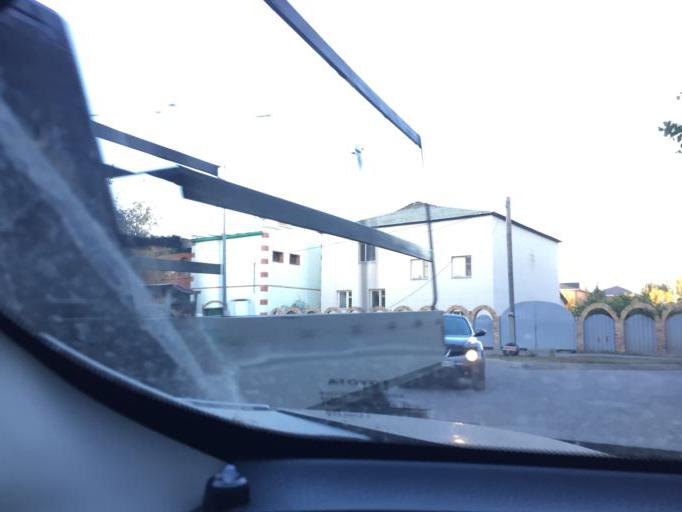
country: KZ
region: Astana Qalasy
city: Astana
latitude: 51.1473
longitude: 71.4271
